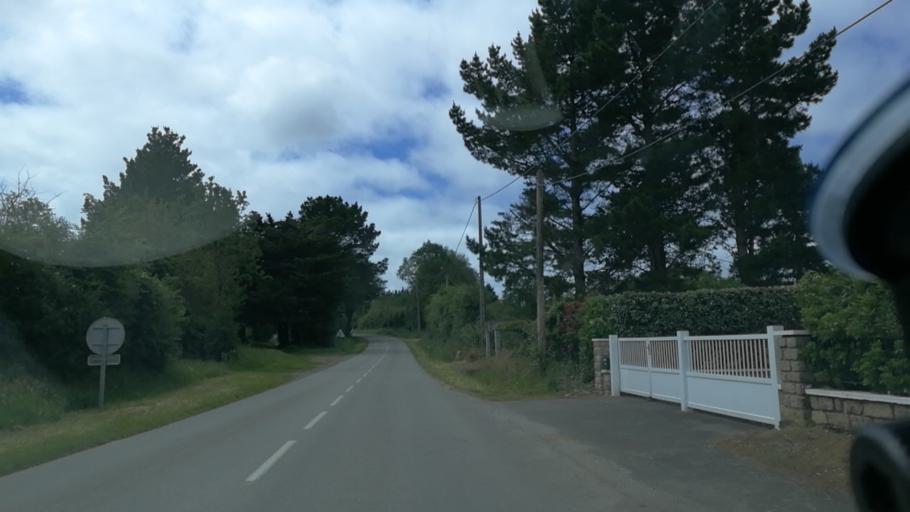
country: FR
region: Brittany
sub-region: Departement du Morbihan
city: Penestin
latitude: 47.4891
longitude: -2.4362
